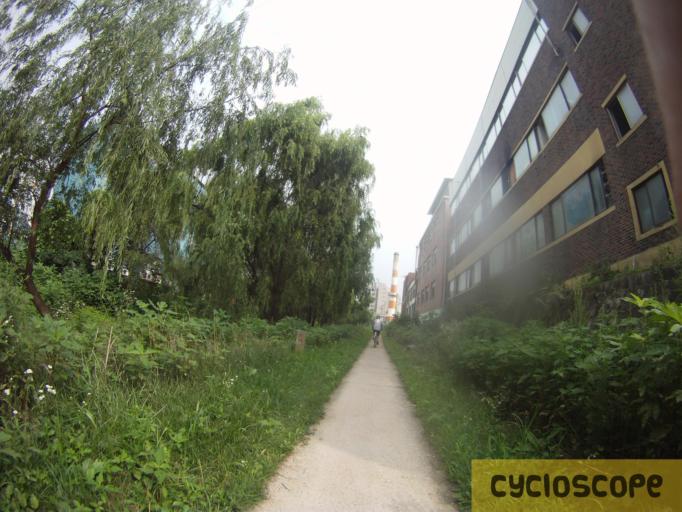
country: KR
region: Gyeonggi-do
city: Anyang-si
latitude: 37.3471
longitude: 126.9734
